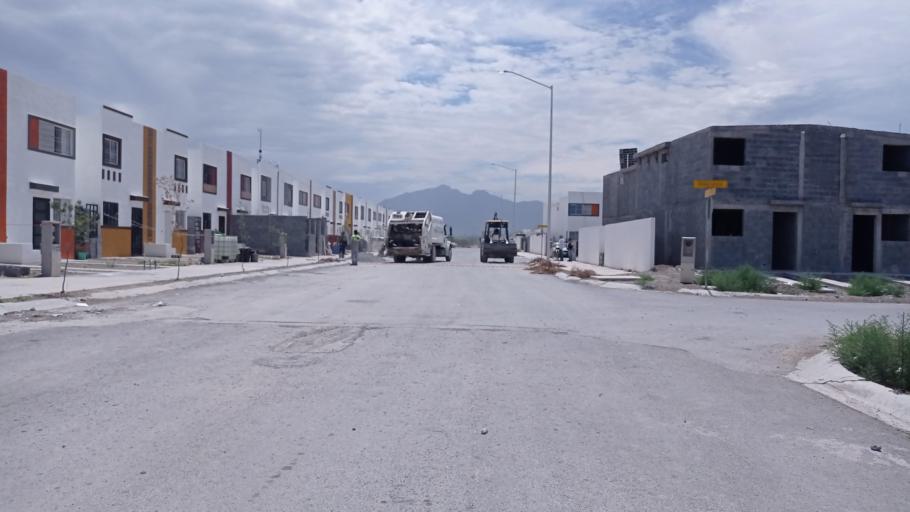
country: MX
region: Nuevo Leon
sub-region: Salinas Victoria
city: Simeprodeso (Colectivo Nuevo)
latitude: 25.8742
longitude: -100.3187
